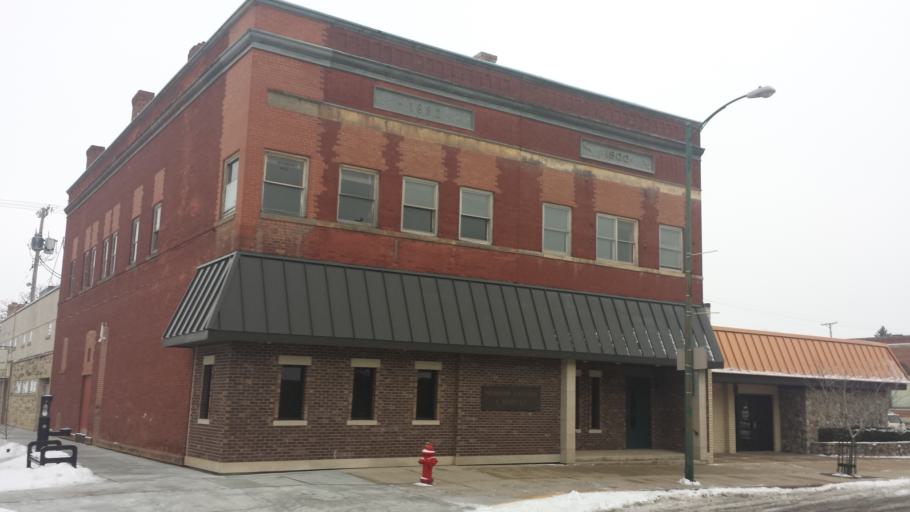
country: US
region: Wisconsin
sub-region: Monroe County
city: Tomah
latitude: 43.9773
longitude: -90.5047
